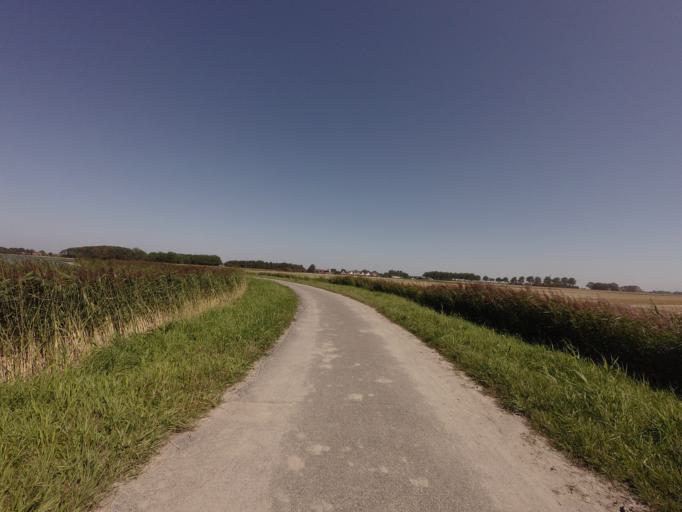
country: NL
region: Friesland
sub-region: Gemeente Dongeradeel
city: Anjum
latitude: 53.3973
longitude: 6.0771
